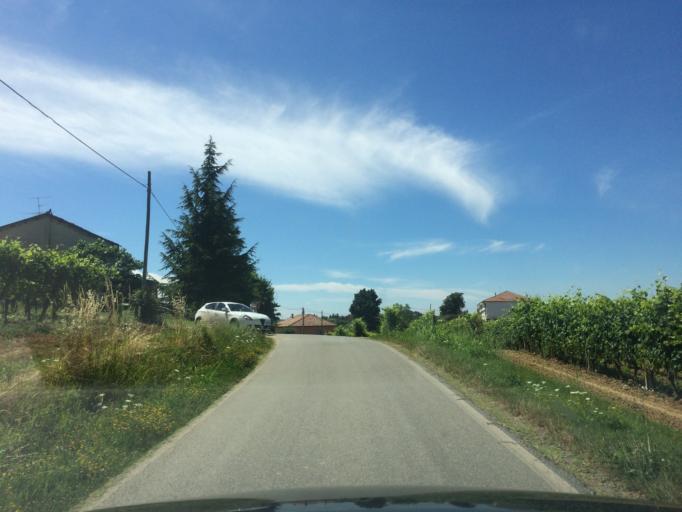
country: IT
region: Piedmont
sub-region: Provincia di Asti
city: Vaglio Serra
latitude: 44.7780
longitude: 8.3253
